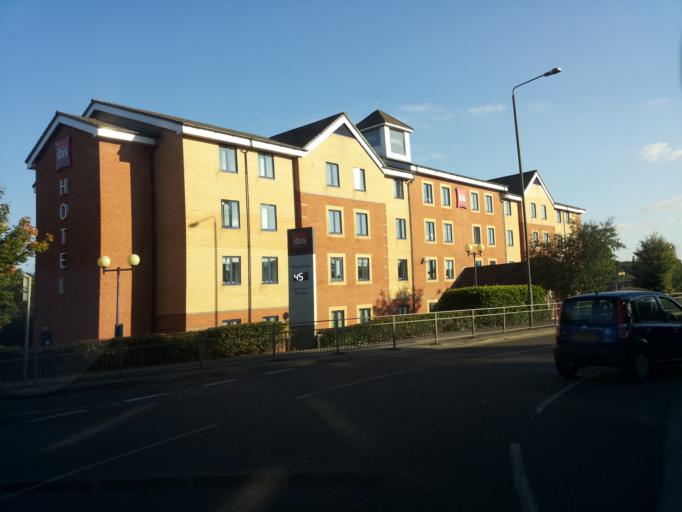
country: GB
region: England
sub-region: Derbyshire
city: Chesterfield
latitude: 53.2334
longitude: -1.4240
